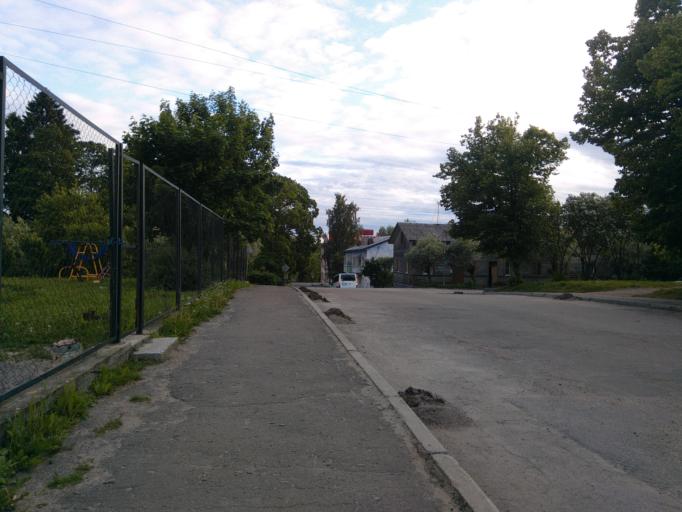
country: RU
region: Republic of Karelia
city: Sortavala
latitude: 61.7045
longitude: 30.6870
